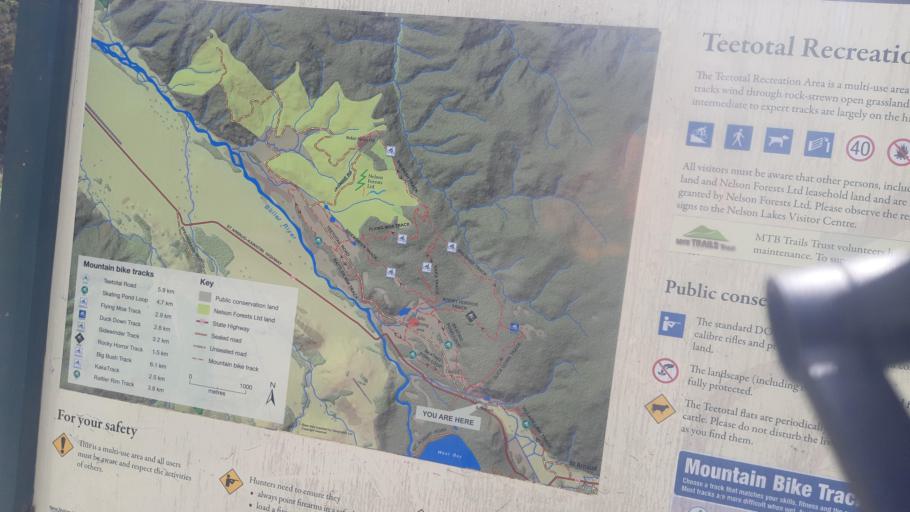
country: NZ
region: Tasman
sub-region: Tasman District
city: Wakefield
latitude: -41.7929
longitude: 172.8335
